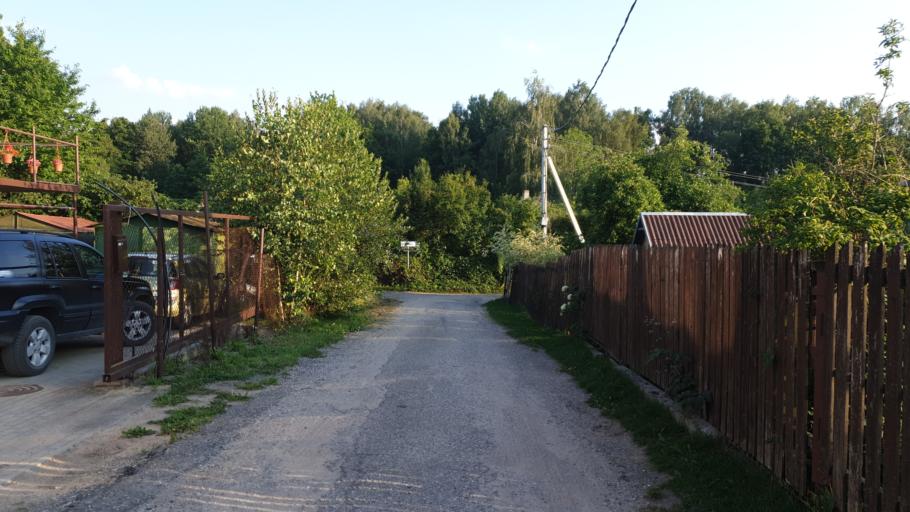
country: LT
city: Grigiskes
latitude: 54.7626
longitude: 25.0300
